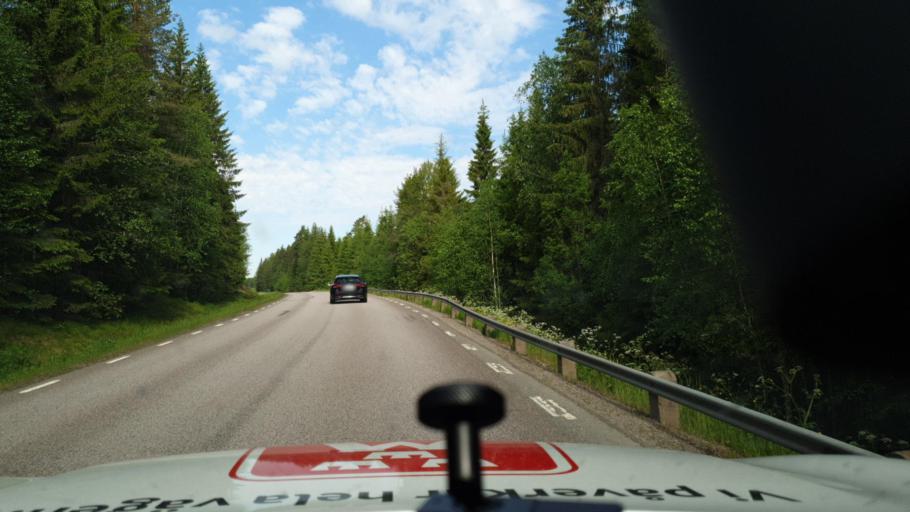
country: SE
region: Vaermland
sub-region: Eda Kommun
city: Charlottenberg
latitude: 59.8842
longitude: 12.3649
